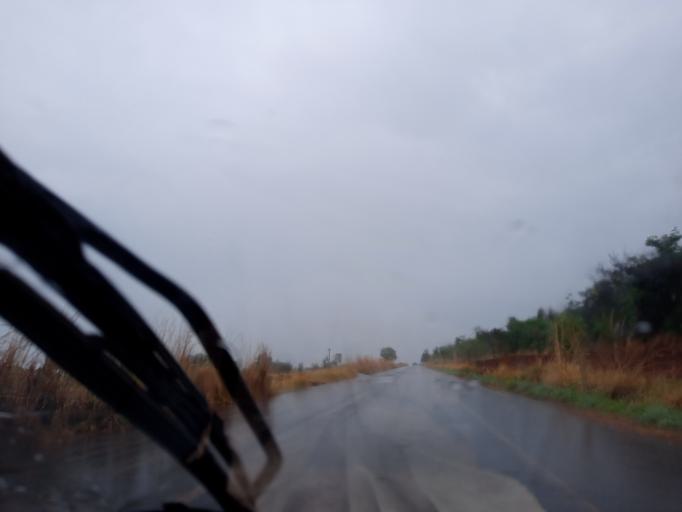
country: BR
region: Minas Gerais
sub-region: Ituiutaba
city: Ituiutaba
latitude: -19.0588
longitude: -49.5044
